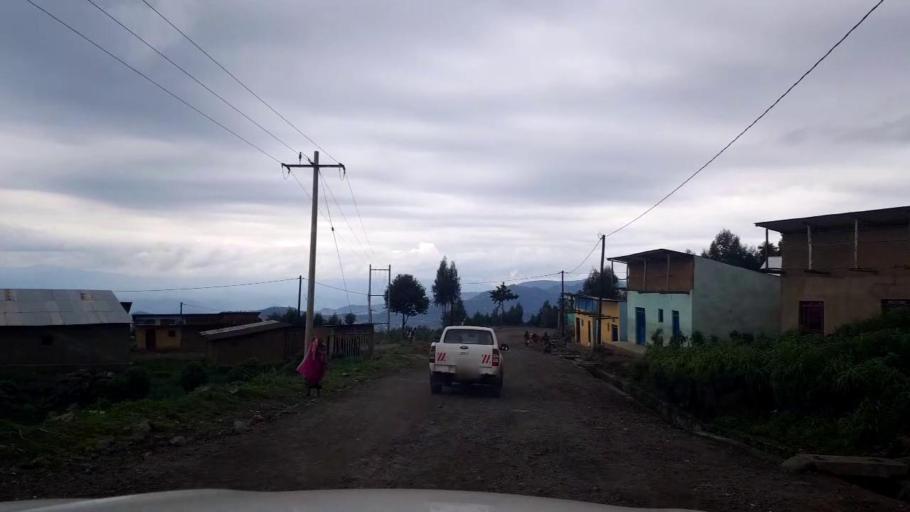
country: RW
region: Northern Province
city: Musanze
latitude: -1.4933
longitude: 29.5320
